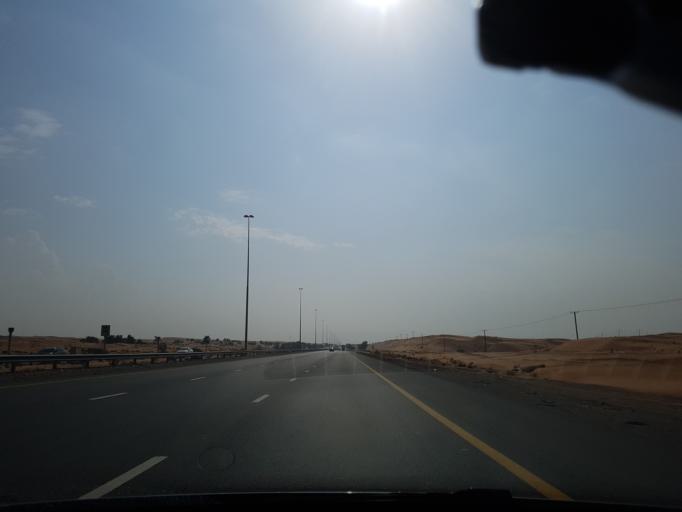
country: AE
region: Umm al Qaywayn
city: Umm al Qaywayn
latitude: 25.5152
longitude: 55.7083
